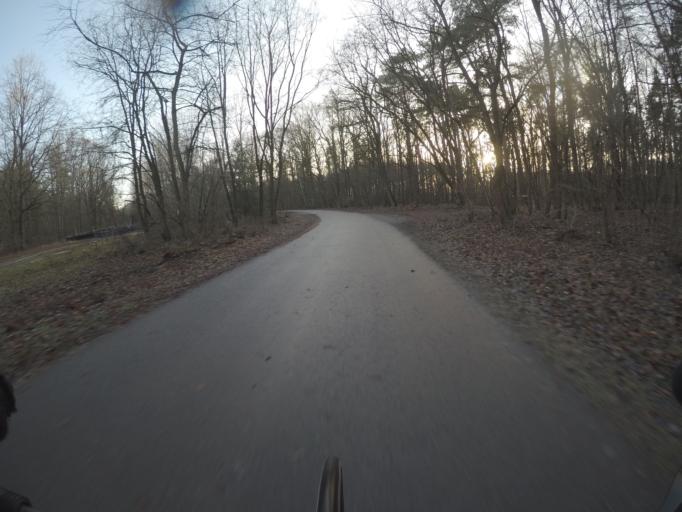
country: DE
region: Brandenburg
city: Hennigsdorf
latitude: 52.6550
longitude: 13.2213
